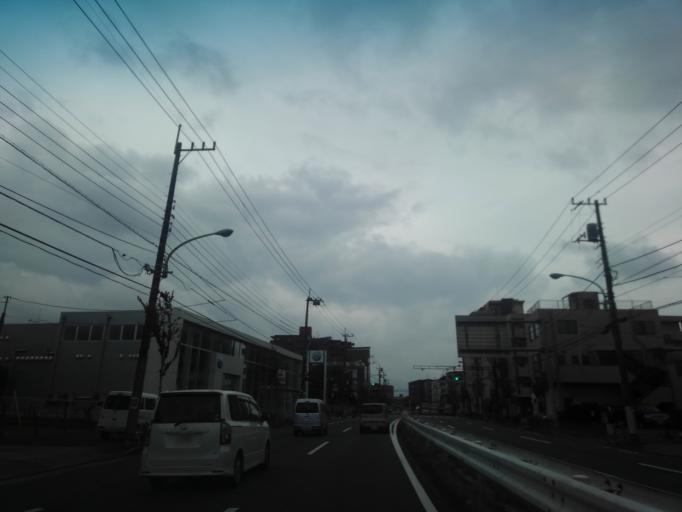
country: JP
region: Tokyo
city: Musashino
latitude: 35.7241
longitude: 139.5612
